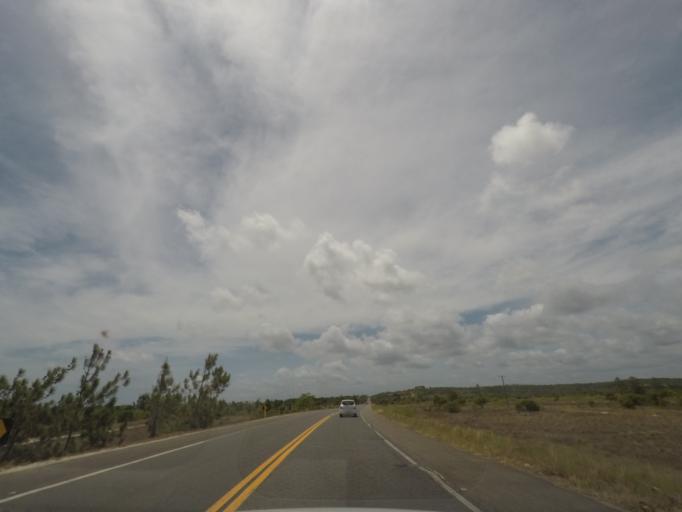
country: BR
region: Bahia
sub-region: Conde
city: Conde
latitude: -11.8702
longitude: -37.6338
